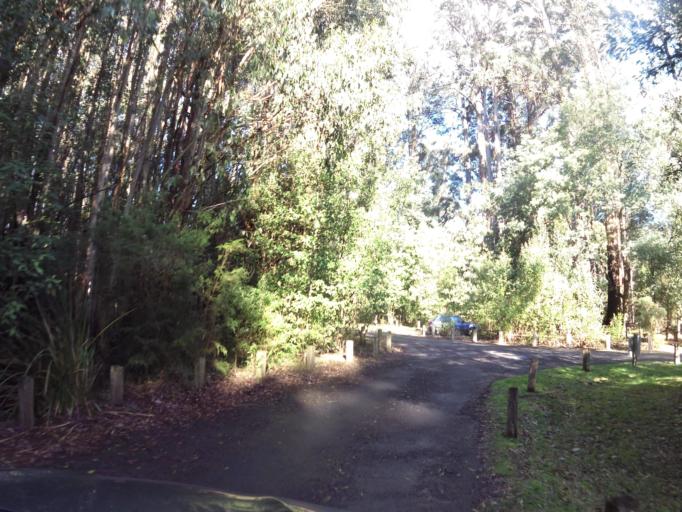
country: AU
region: Victoria
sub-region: Yarra Ranges
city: Kallista
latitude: -37.8835
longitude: 145.3576
